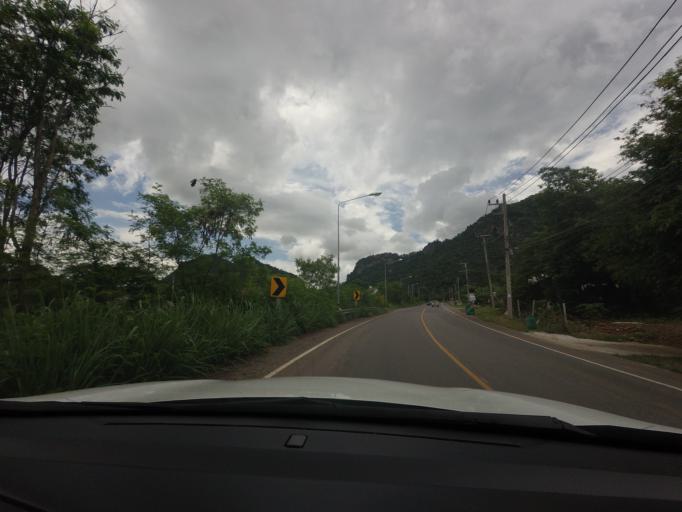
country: TH
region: Sara Buri
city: Muak Lek
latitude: 14.5482
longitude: 101.3260
